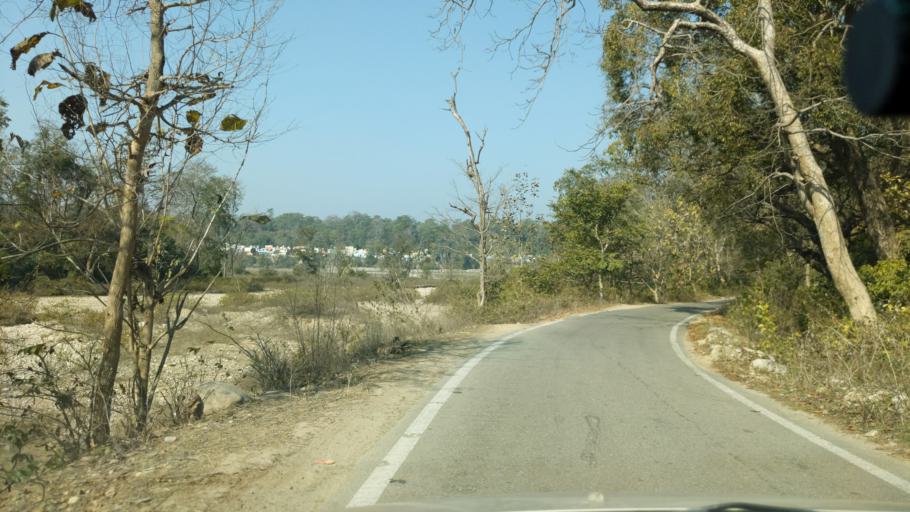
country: IN
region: Uttarakhand
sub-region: Naini Tal
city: Ramnagar
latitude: 29.4081
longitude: 79.1379
